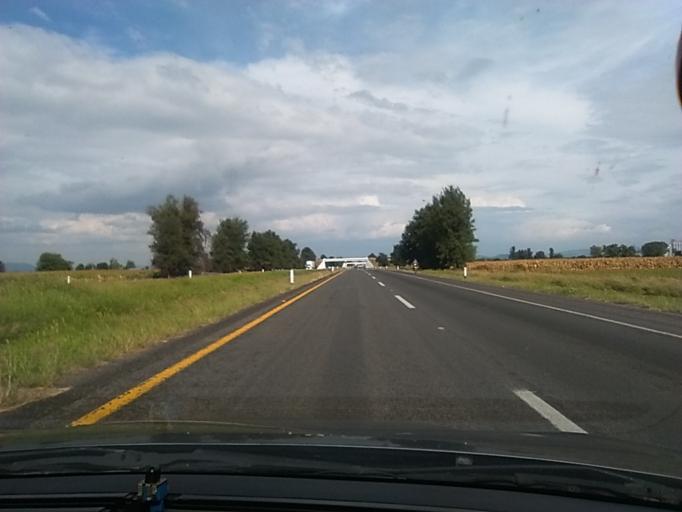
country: MX
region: Jalisco
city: La Barca
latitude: 20.3220
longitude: -102.5319
